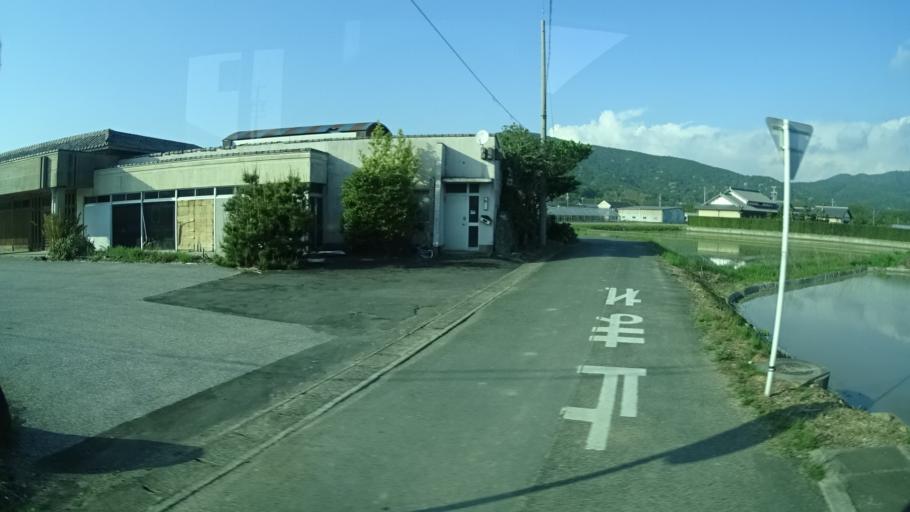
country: JP
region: Aichi
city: Tahara
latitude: 34.6570
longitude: 137.2005
